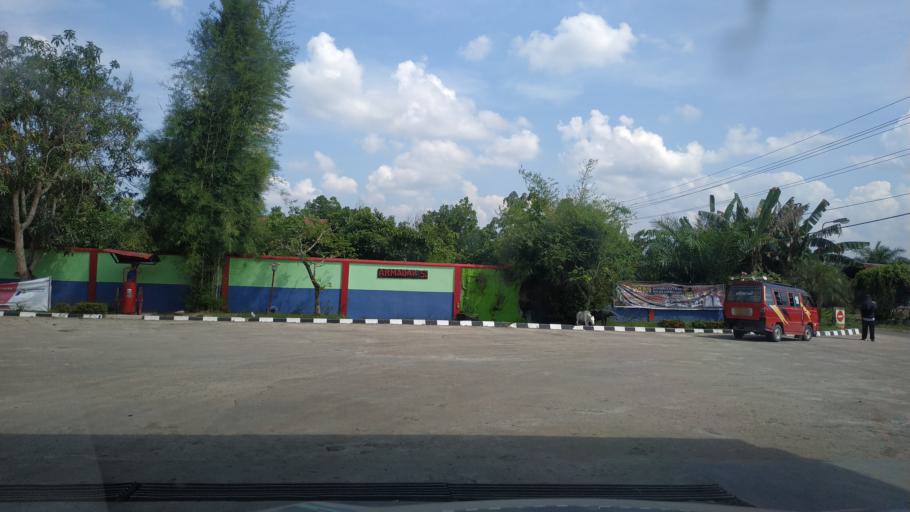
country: ID
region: North Sumatra
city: Binanga
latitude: 1.4171
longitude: 99.7652
